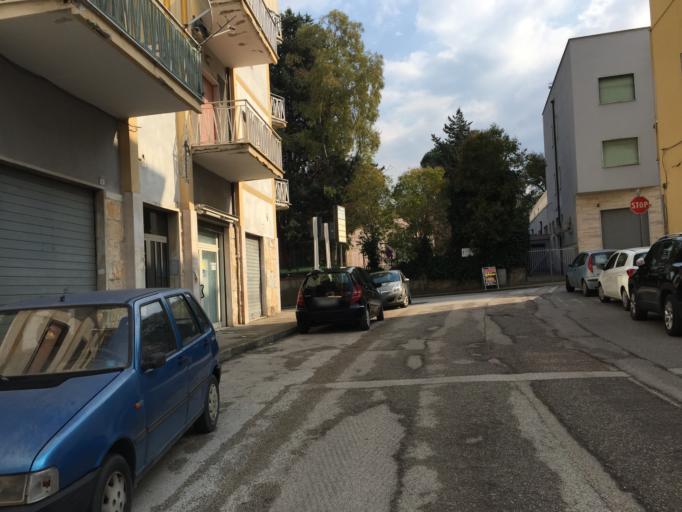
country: IT
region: Campania
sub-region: Provincia di Benevento
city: Benevento
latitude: 41.1346
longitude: 14.7823
